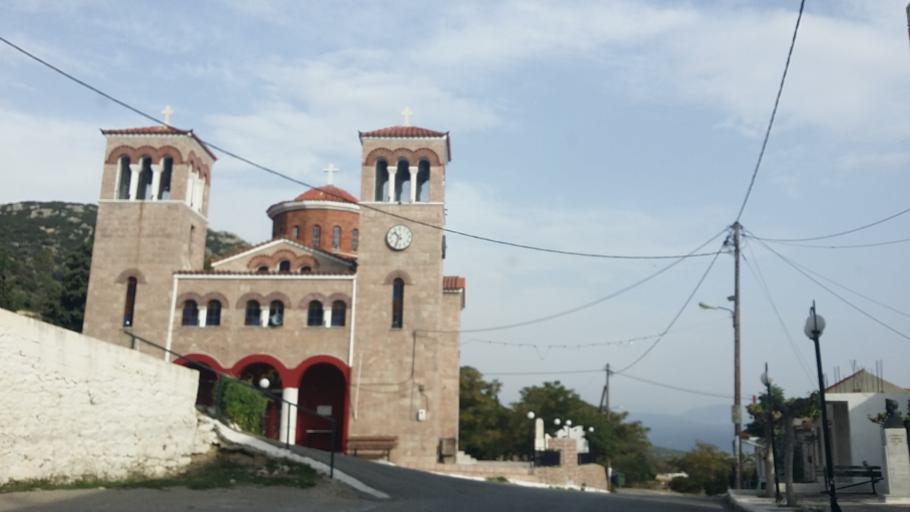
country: GR
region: Central Greece
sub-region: Nomos Voiotias
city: Korini
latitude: 38.2598
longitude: 22.9114
